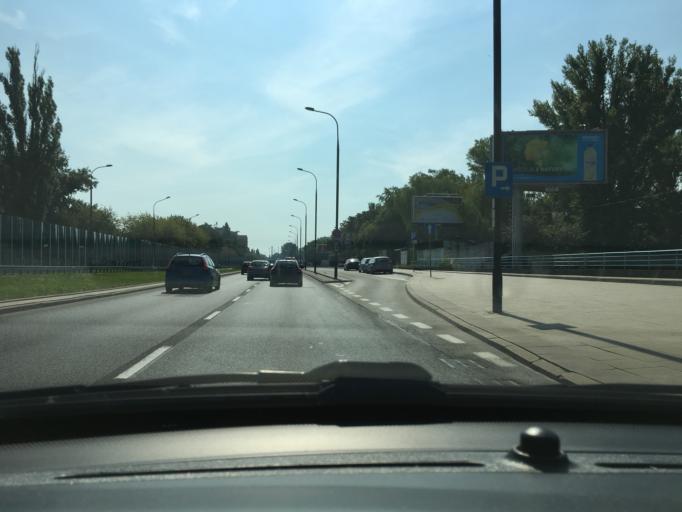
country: PL
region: Masovian Voivodeship
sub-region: Warszawa
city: Praga Polnoc
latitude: 52.2339
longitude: 21.0473
